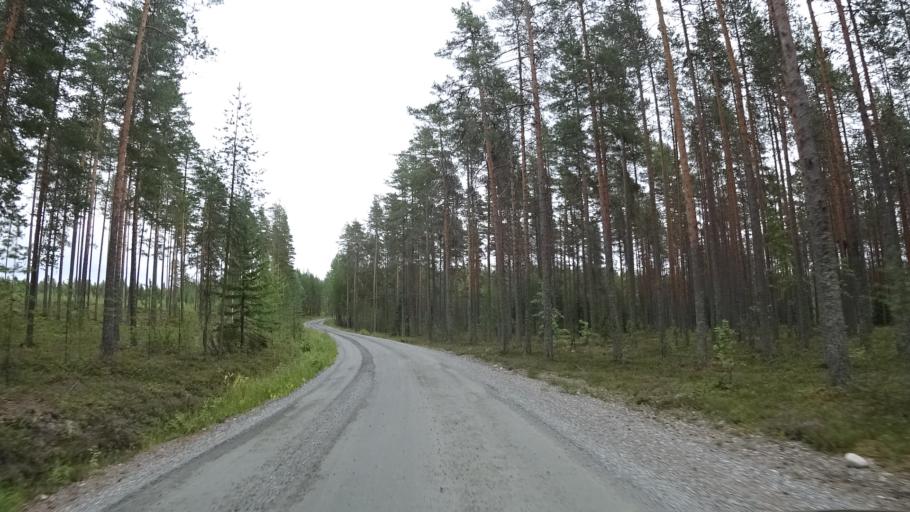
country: FI
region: North Karelia
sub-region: Pielisen Karjala
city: Lieksa
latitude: 63.3777
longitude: 30.3483
